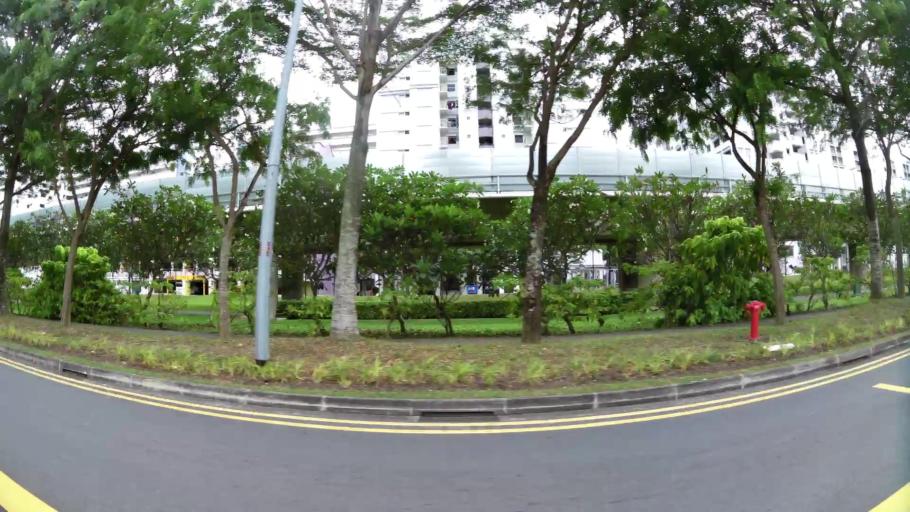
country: MY
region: Johor
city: Johor Bahru
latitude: 1.4398
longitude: 103.7985
